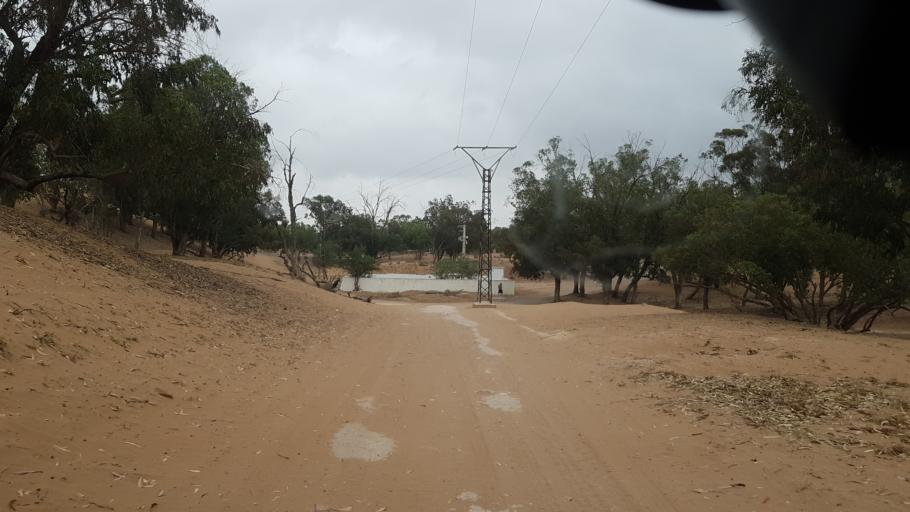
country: MA
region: Souss-Massa-Draa
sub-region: Inezgane-Ait Mellou
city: Inezgane
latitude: 30.3177
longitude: -9.5376
